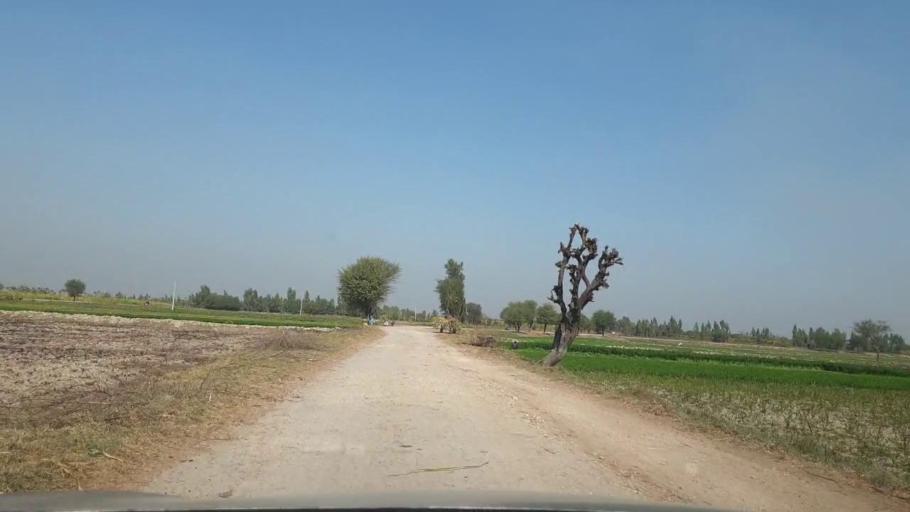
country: PK
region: Sindh
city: Tando Adam
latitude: 25.6060
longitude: 68.6423
